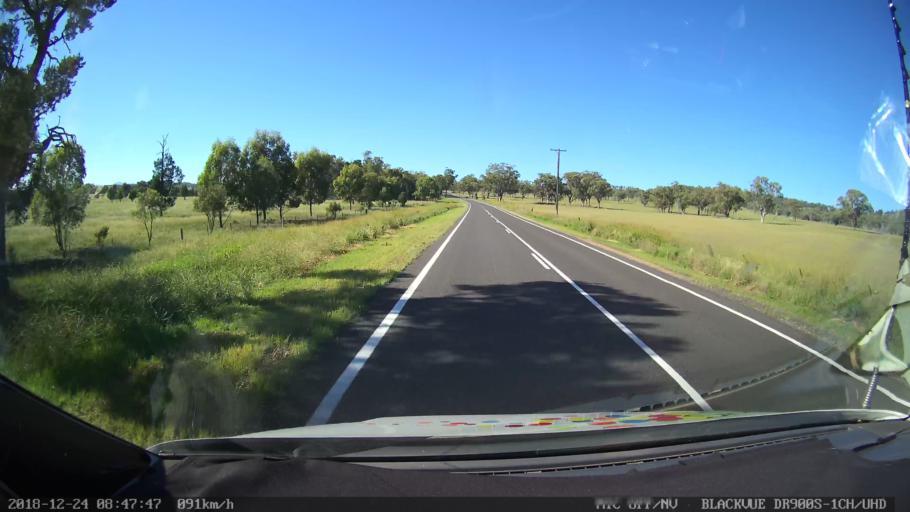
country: AU
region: New South Wales
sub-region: Liverpool Plains
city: Quirindi
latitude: -31.4469
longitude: 150.6467
